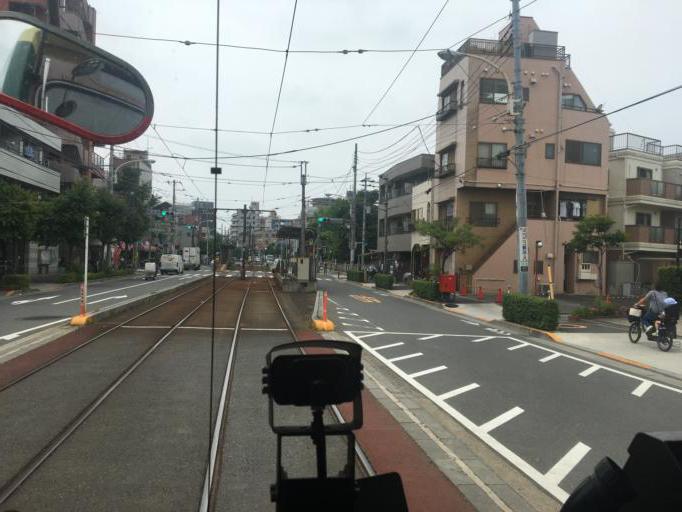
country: JP
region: Saitama
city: Kawaguchi
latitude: 35.7499
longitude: 139.7659
